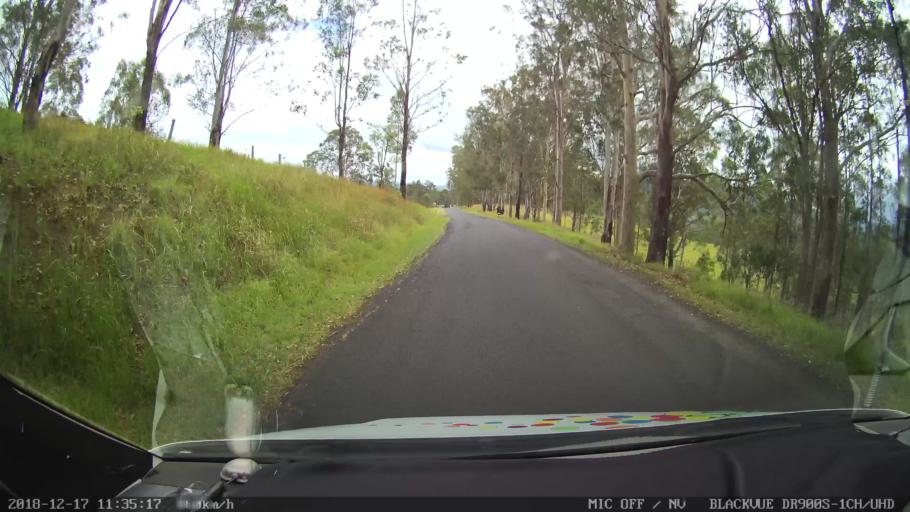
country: AU
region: New South Wales
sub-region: Kyogle
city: Kyogle
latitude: -28.7243
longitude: 152.6070
